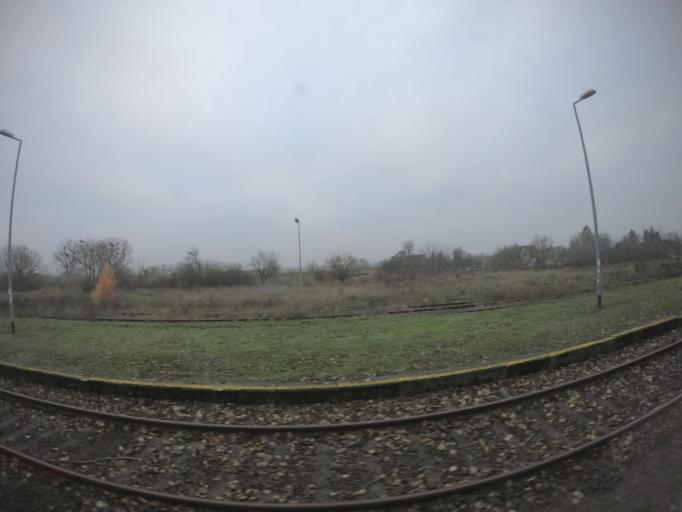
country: PL
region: Lubusz
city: Gorzow Wielkopolski
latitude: 52.7174
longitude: 15.1804
